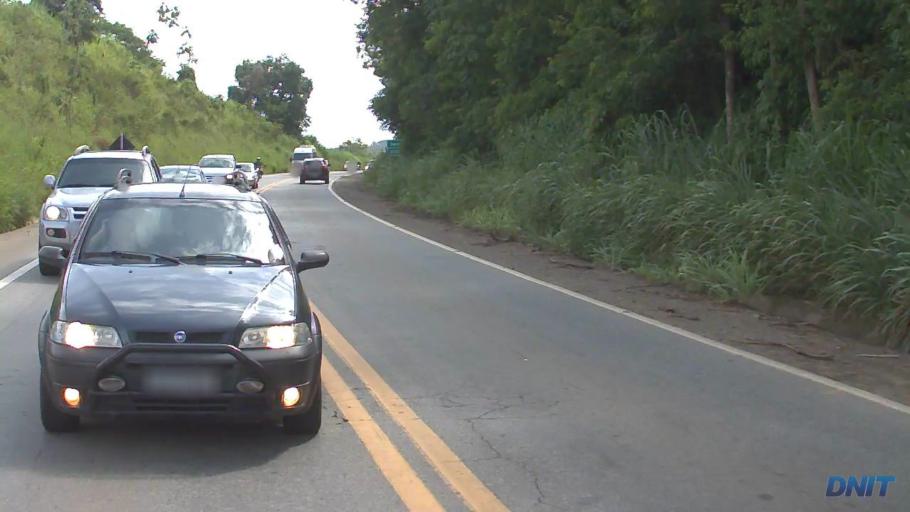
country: BR
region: Minas Gerais
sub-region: Ipaba
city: Ipaba
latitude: -19.3723
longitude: -42.4590
